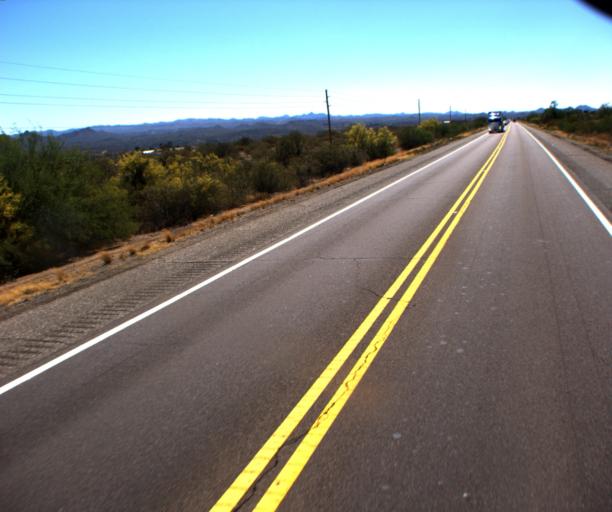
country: US
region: Arizona
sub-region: Maricopa County
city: Wickenburg
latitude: 34.0110
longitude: -112.7880
